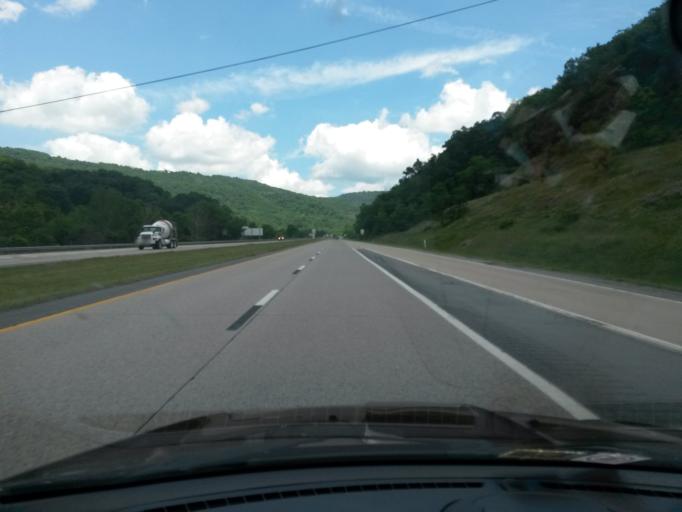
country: US
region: West Virginia
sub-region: Summers County
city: Hinton
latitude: 37.8092
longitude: -80.8150
